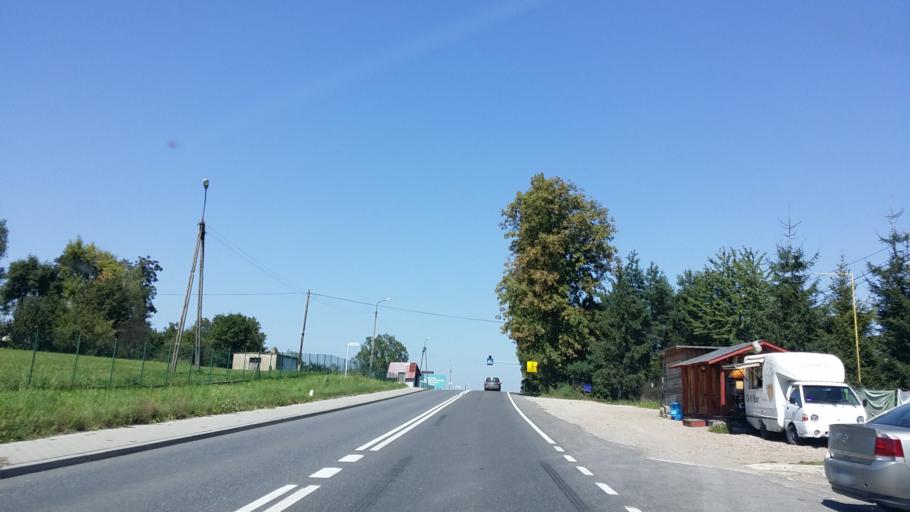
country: PL
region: Lesser Poland Voivodeship
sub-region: Powiat wadowicki
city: Radocza
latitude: 49.9125
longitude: 19.4833
